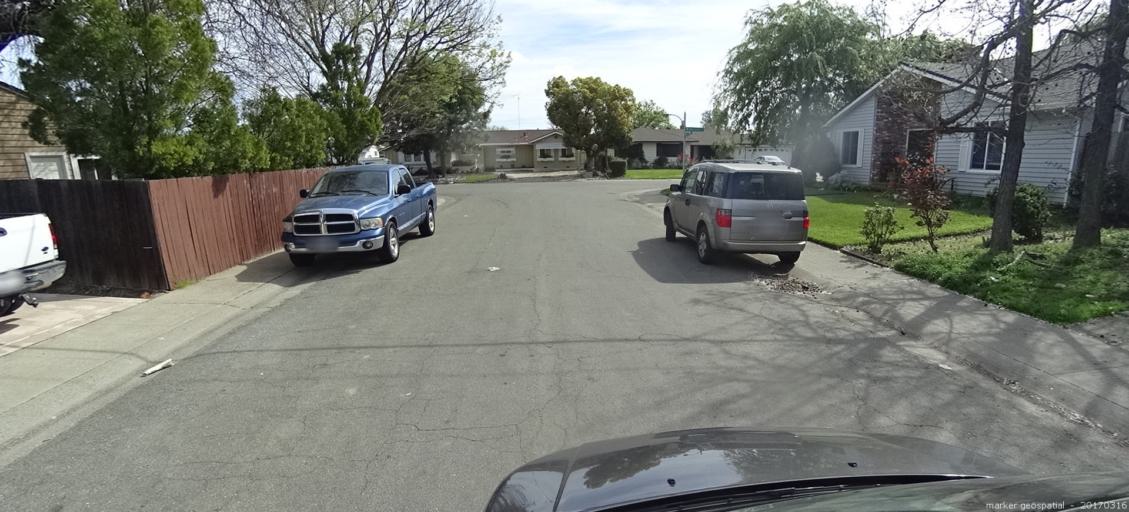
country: US
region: California
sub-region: Sacramento County
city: Parkway
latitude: 38.5001
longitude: -121.4856
